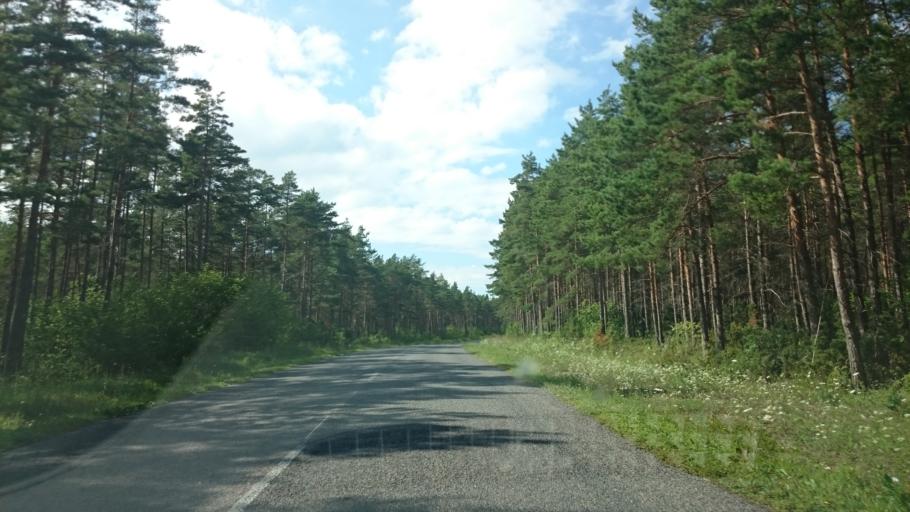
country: EE
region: Saare
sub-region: Orissaare vald
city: Orissaare
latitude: 58.5919
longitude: 23.0096
